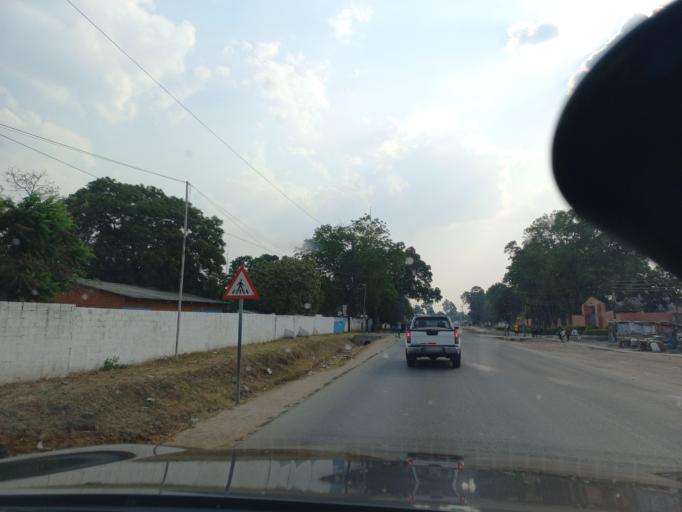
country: ZM
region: Lusaka
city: Lusaka
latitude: -15.4626
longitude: 28.2454
